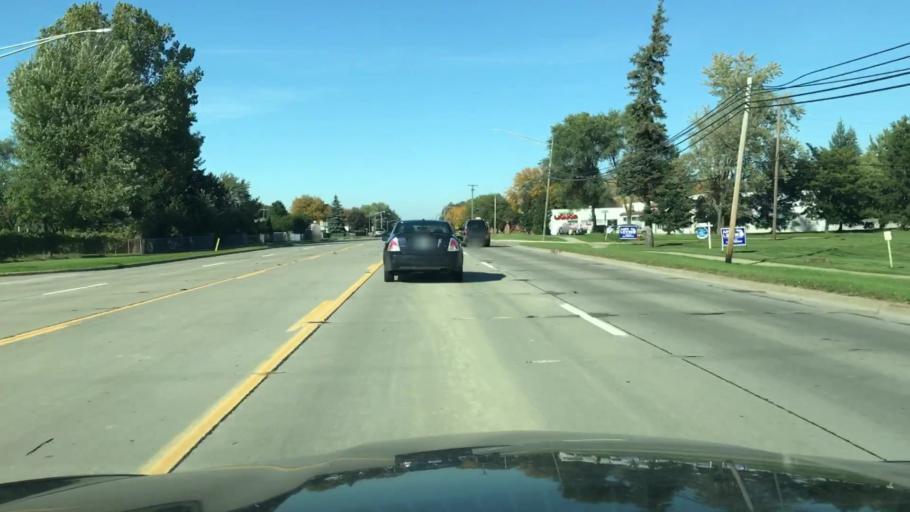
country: US
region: Michigan
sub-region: Oakland County
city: Clawson
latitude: 42.5541
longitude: -83.0883
